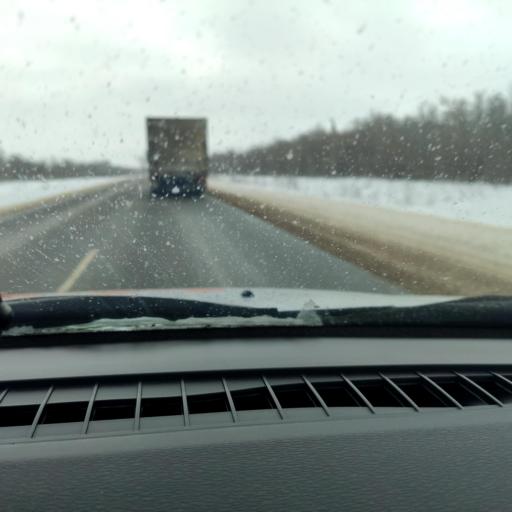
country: RU
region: Samara
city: Dubovyy Umet
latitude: 52.7653
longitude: 50.4931
